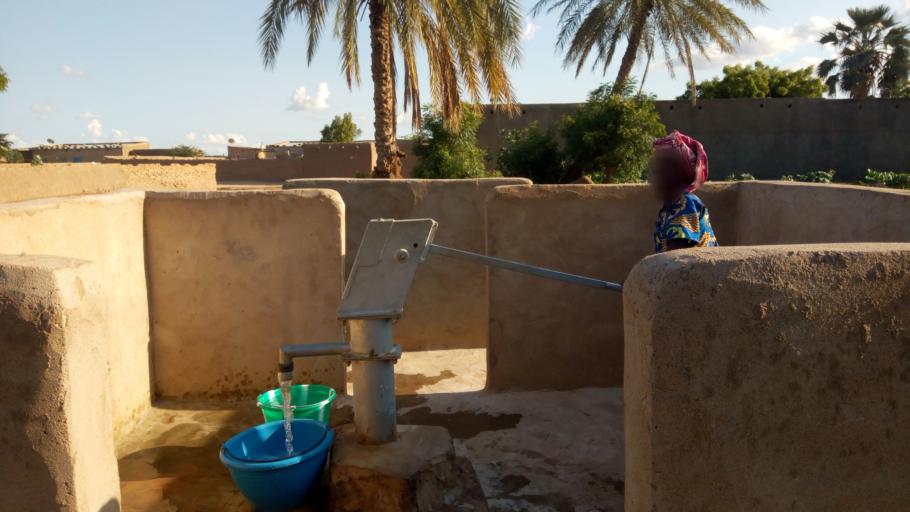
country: ML
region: Segou
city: Niono
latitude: 14.3095
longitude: -5.9566
